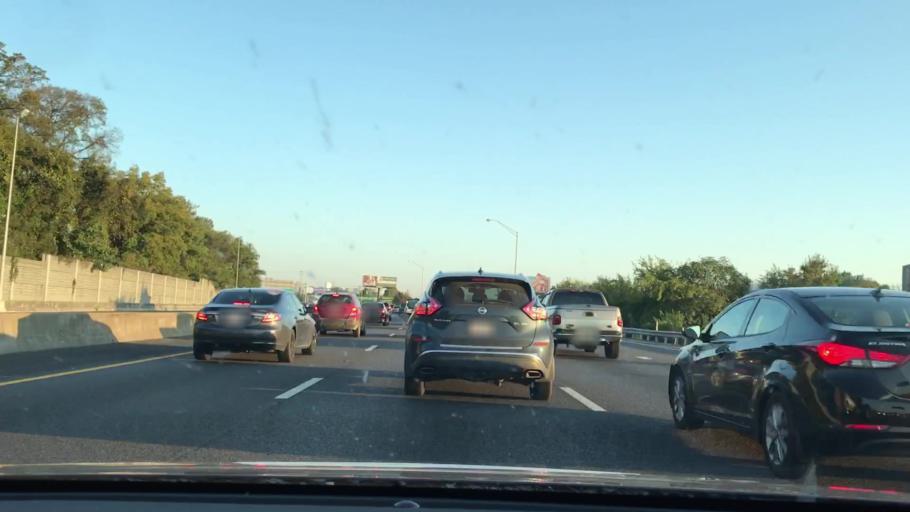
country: US
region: Tennessee
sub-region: Davidson County
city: Nashville
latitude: 36.1277
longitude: -86.7726
